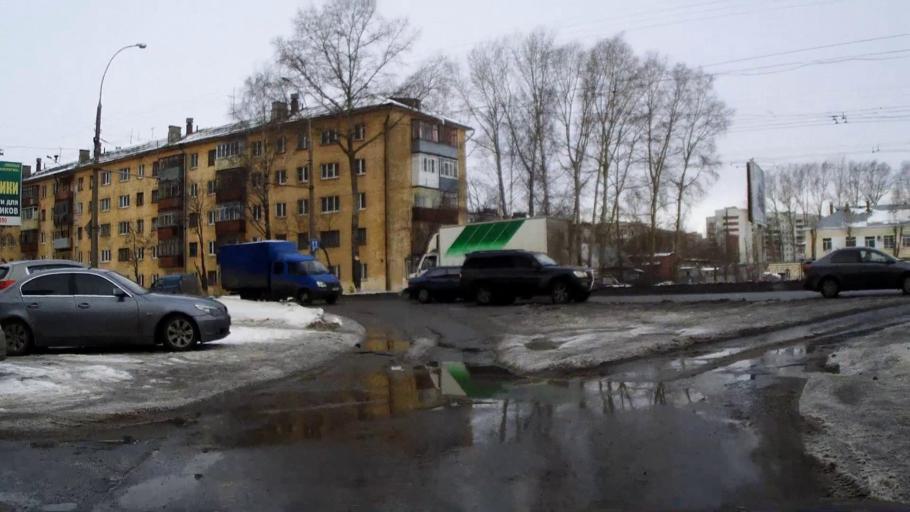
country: RU
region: Vologda
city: Vologda
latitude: 59.2142
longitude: 39.8577
